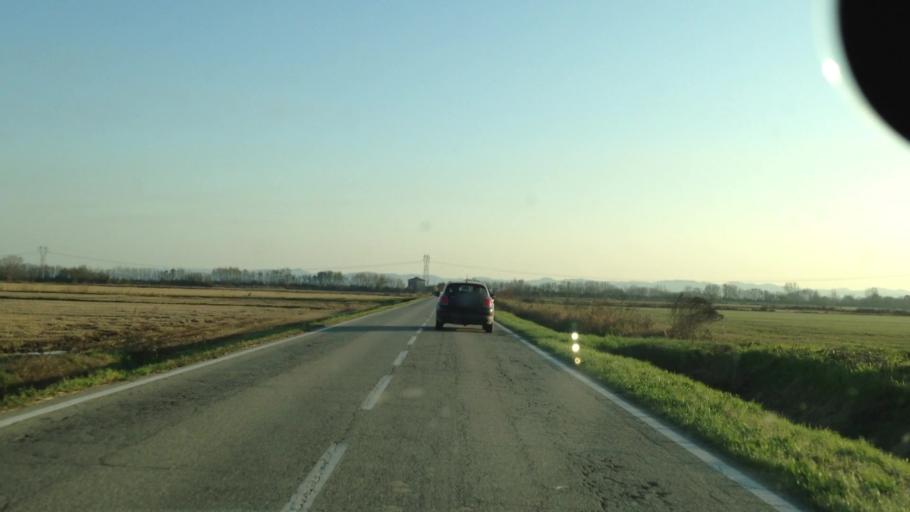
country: IT
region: Piedmont
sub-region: Provincia di Vercelli
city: Lamporo
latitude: 45.2519
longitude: 8.0878
